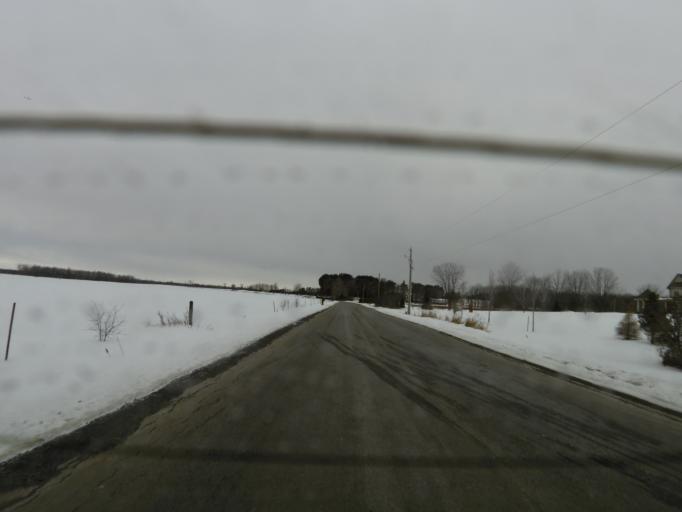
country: CA
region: Ontario
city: Clarence-Rockland
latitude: 45.4130
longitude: -75.4477
